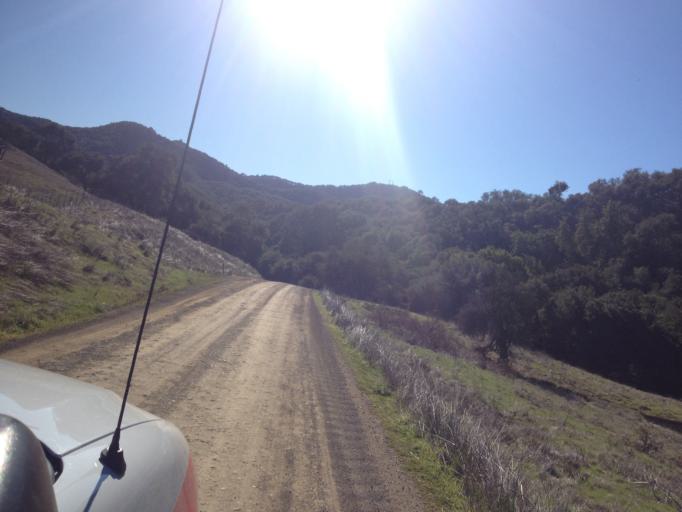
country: US
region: California
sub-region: San Luis Obispo County
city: Avila Beach
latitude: 35.2487
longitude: -120.7769
